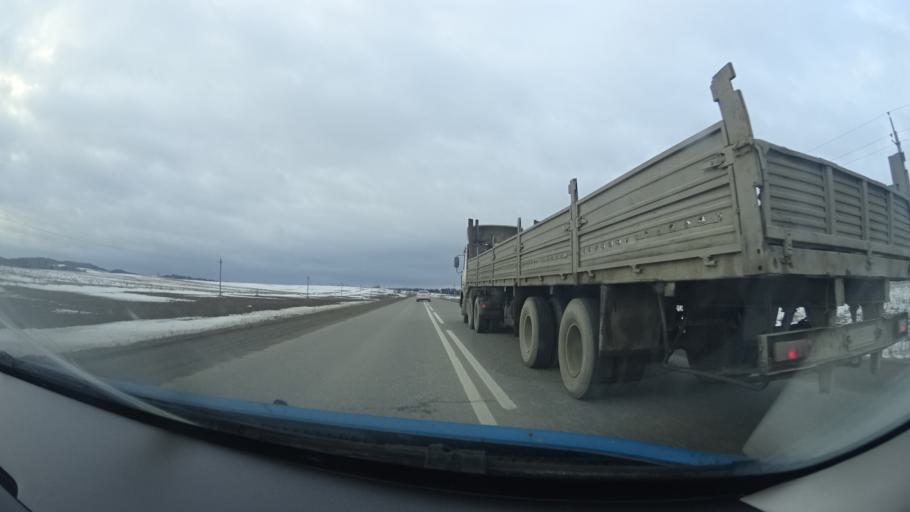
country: RU
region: Perm
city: Osa
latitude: 57.2454
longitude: 55.5922
